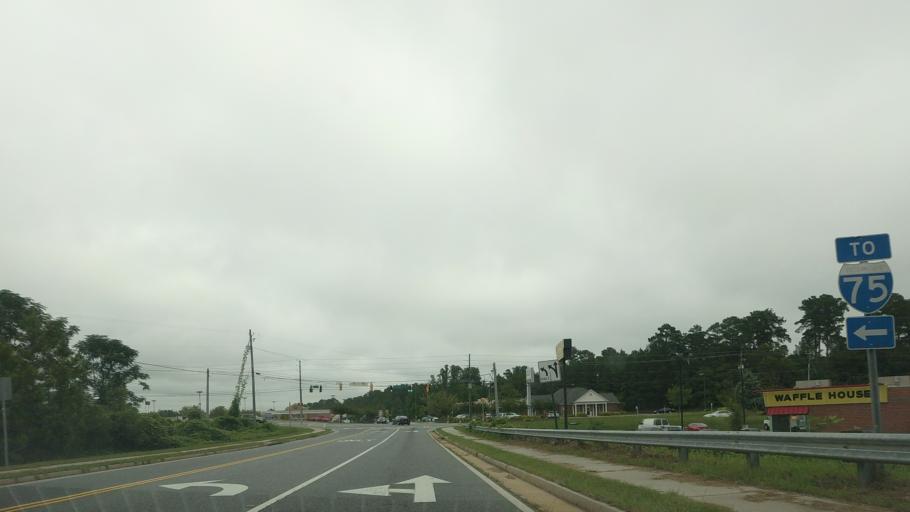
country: US
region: Georgia
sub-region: Peach County
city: Byron
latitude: 32.7422
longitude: -83.7142
